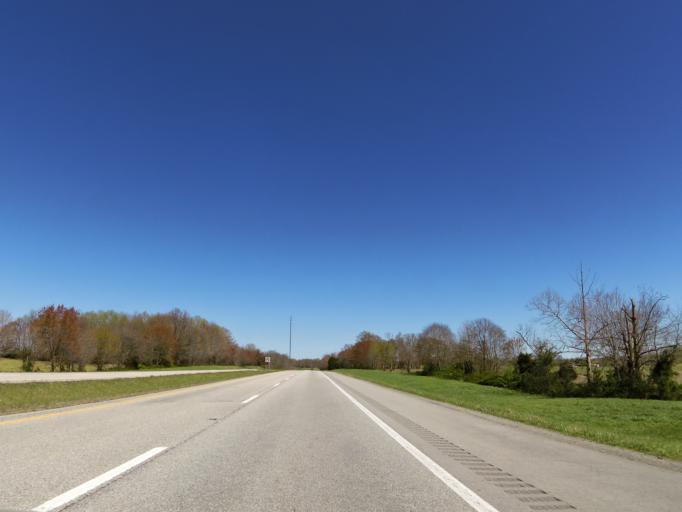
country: US
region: Kentucky
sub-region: Russell County
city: Russell Springs
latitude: 37.0863
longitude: -84.9240
